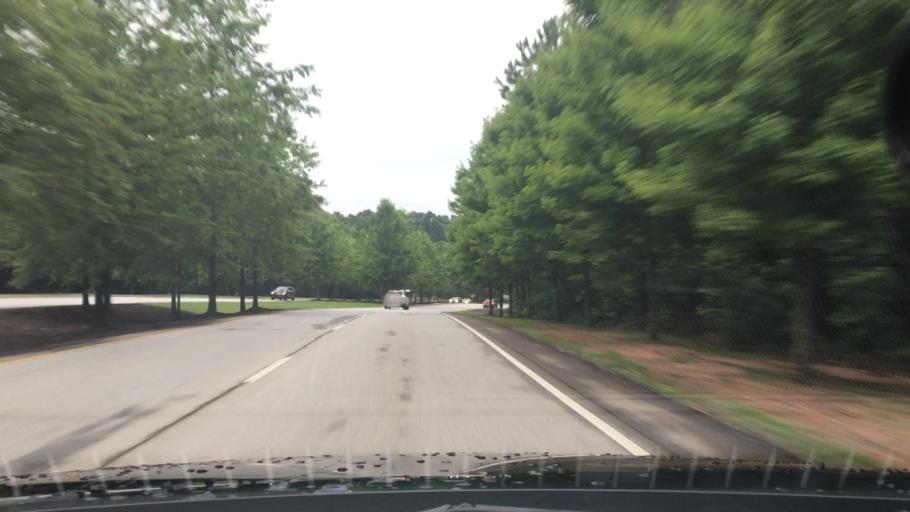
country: US
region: Georgia
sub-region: Coweta County
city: East Newnan
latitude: 33.3892
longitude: -84.7454
